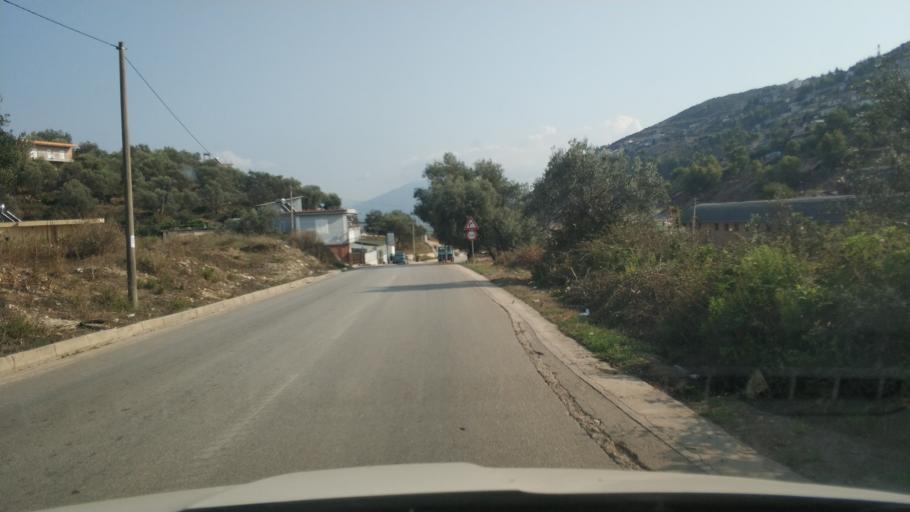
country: AL
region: Vlore
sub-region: Rrethi i Sarandes
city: Sarande
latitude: 39.8724
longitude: 20.0306
